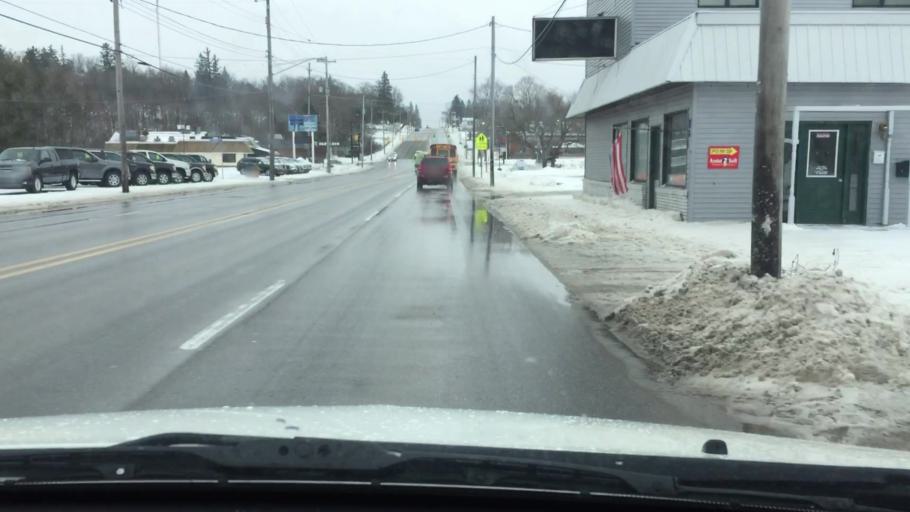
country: US
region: Michigan
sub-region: Wexford County
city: Cadillac
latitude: 44.2428
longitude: -85.3965
